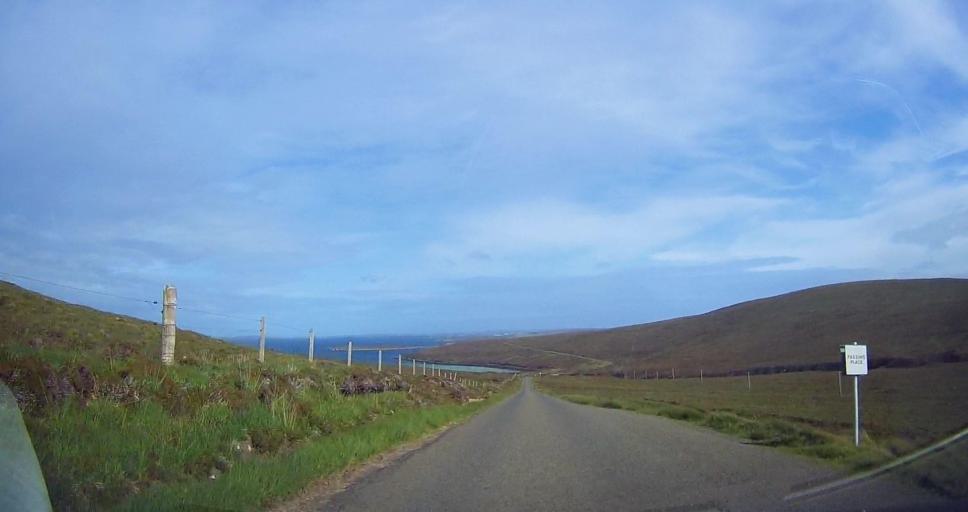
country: GB
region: Scotland
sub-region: Orkney Islands
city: Stromness
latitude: 58.8745
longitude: -3.2437
